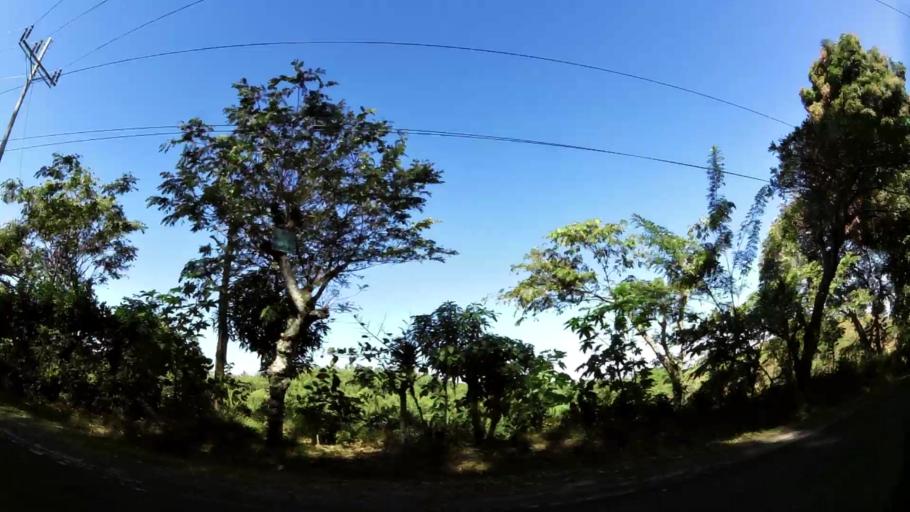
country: SV
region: Ahuachapan
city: Concepcion de Ataco
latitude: 13.8944
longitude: -89.8407
